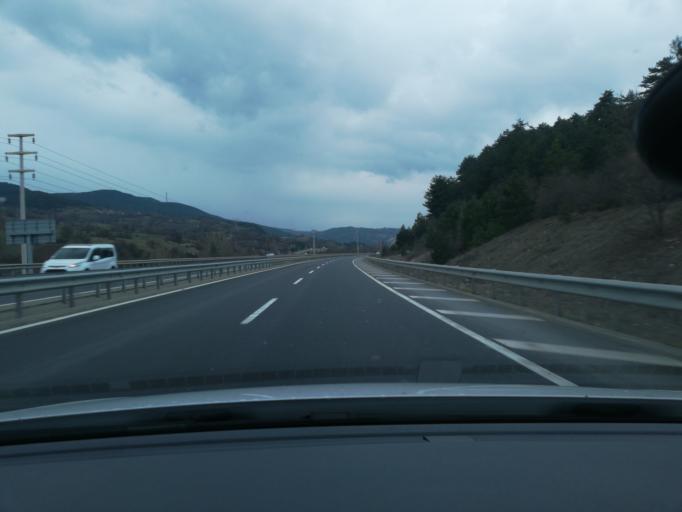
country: TR
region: Bolu
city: Yenicaga
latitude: 40.7432
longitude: 31.8492
